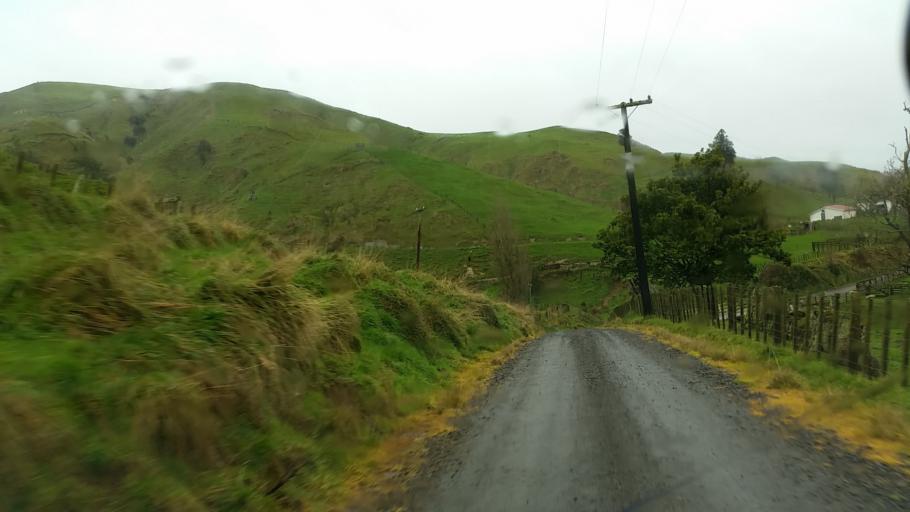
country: NZ
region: Taranaki
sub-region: South Taranaki District
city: Eltham
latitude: -39.4779
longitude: 174.4057
